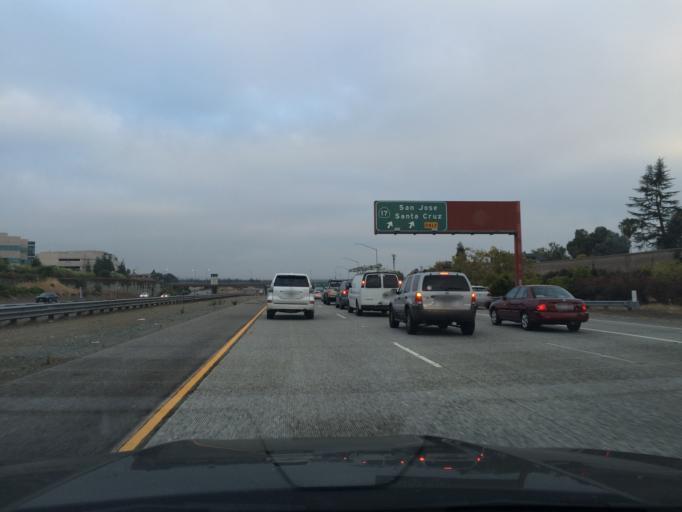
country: US
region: California
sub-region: Santa Clara County
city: Cambrian Park
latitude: 37.2538
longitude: -121.9467
